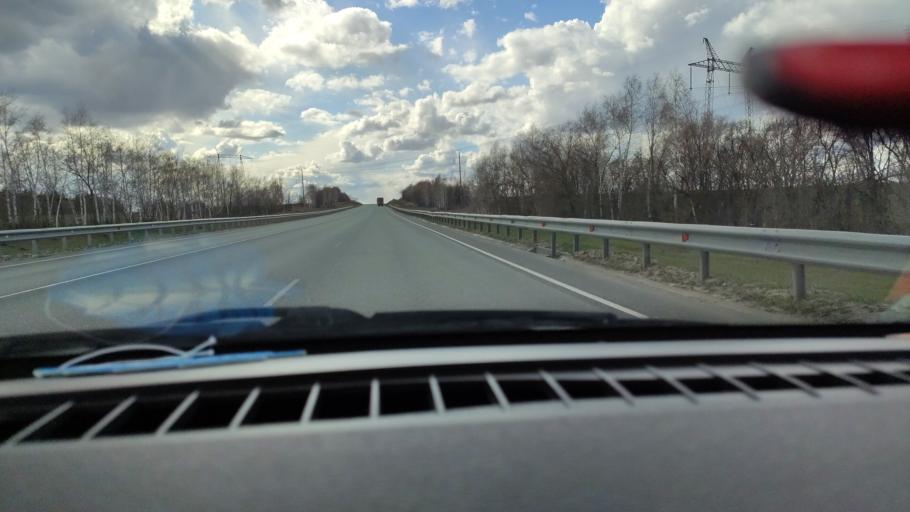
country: RU
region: Saratov
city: Tersa
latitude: 52.1012
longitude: 47.5069
